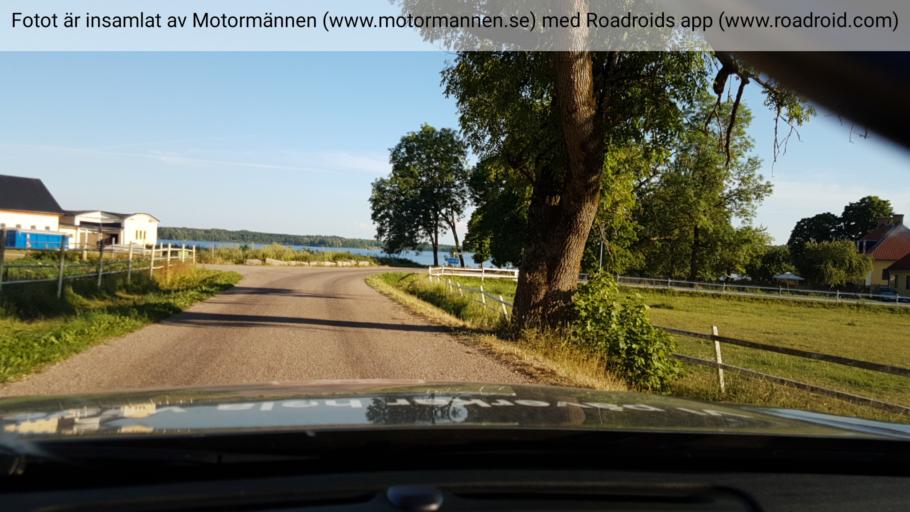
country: SE
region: Vaestmanland
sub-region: Surahammars Kommun
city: Ramnas
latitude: 59.6963
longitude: 16.0658
